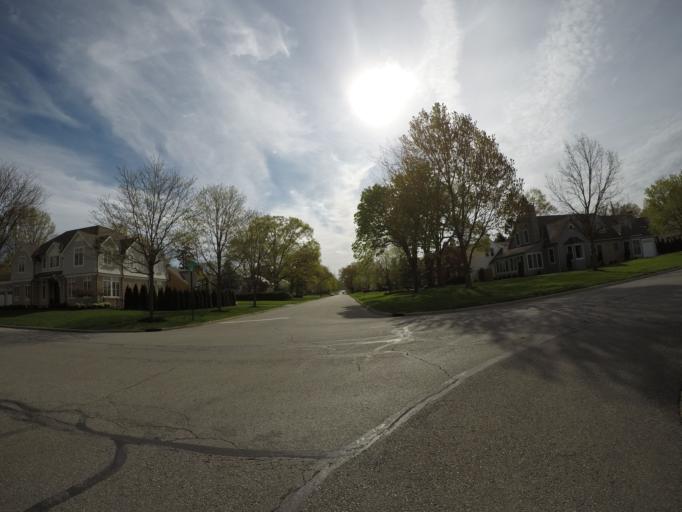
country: US
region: Ohio
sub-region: Franklin County
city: Upper Arlington
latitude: 40.0109
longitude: -83.0765
